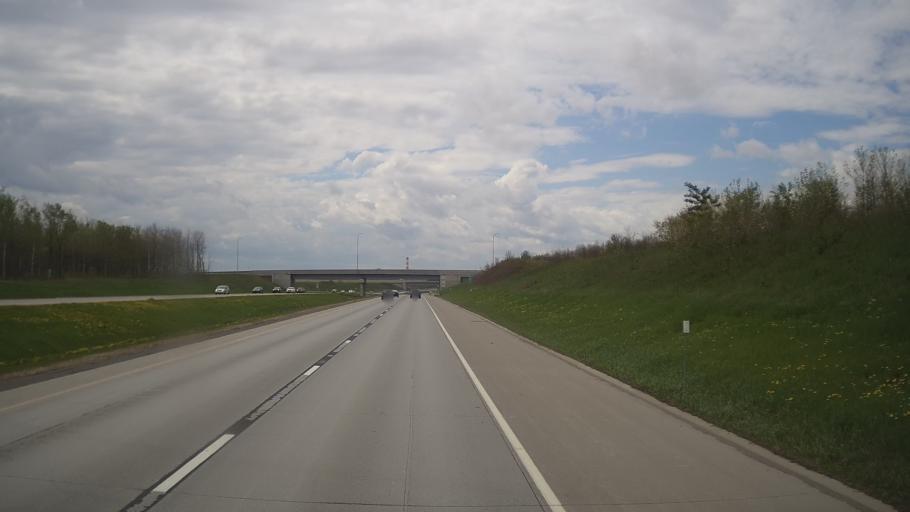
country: CA
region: Quebec
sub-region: Monteregie
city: Candiac
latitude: 45.3657
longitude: -73.5062
